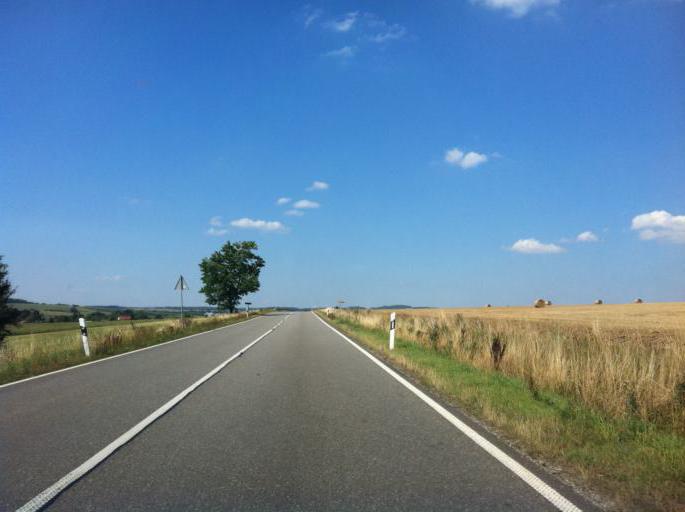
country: DE
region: Thuringia
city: Silberhausen
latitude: 51.3009
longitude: 10.3355
